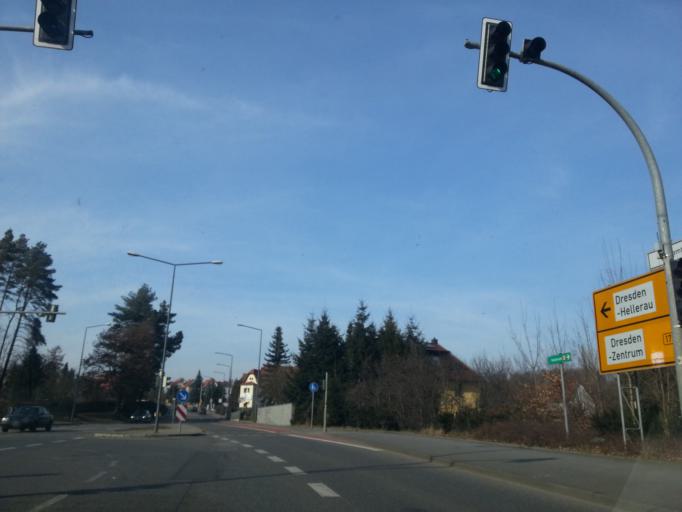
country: DE
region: Saxony
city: Albertstadt
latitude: 51.1085
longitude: 13.7335
